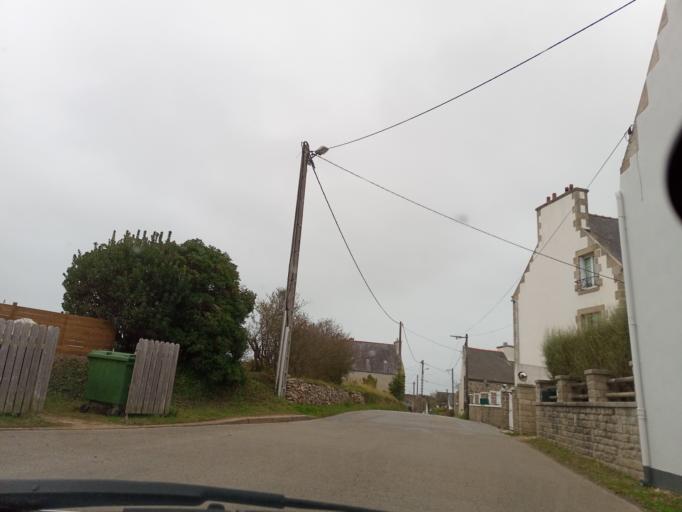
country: FR
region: Brittany
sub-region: Departement du Finistere
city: Esquibien
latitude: 48.0219
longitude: -4.5636
